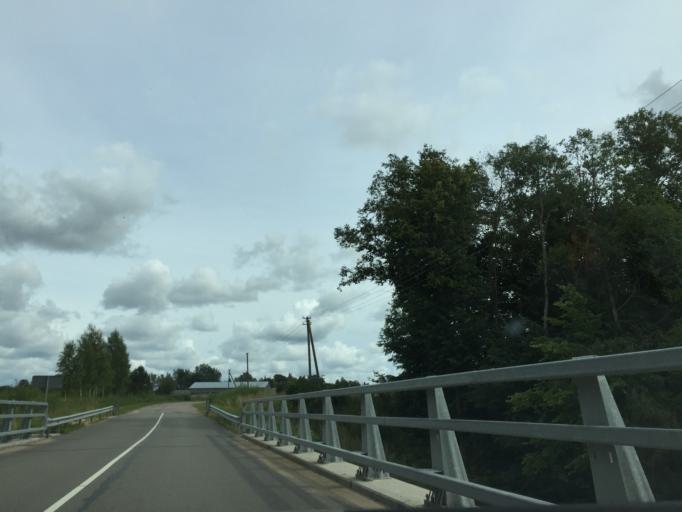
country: LV
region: Lielvarde
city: Lielvarde
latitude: 56.7838
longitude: 24.8979
